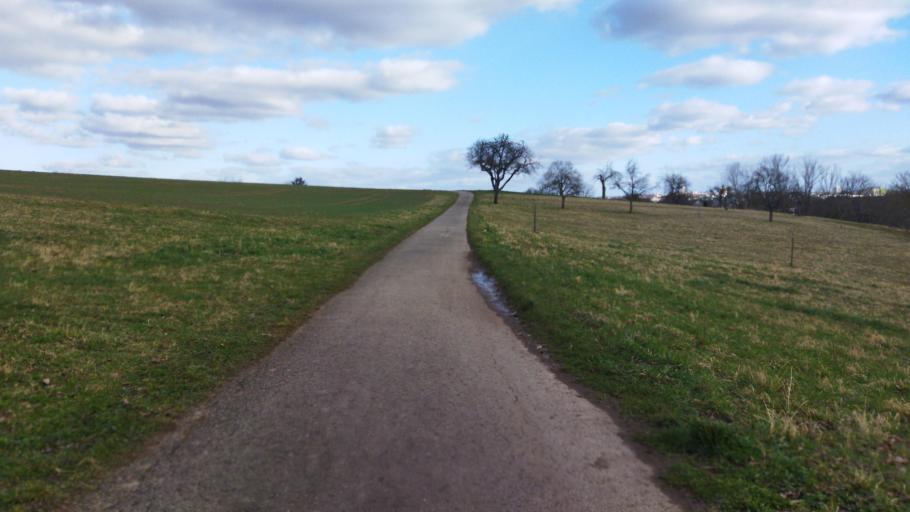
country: DE
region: Baden-Wuerttemberg
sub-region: Regierungsbezirk Stuttgart
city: Bietigheim-Bissingen
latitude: 48.9650
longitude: 9.1069
